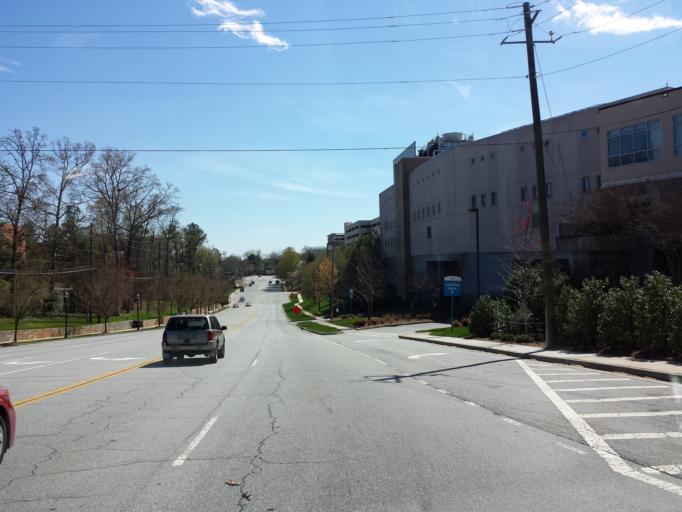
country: US
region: Georgia
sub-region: Fulton County
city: Sandy Springs
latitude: 33.9068
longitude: -84.3530
